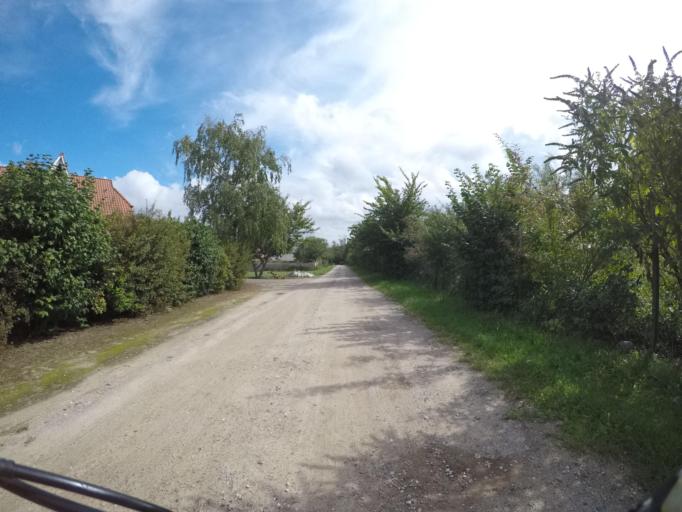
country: DE
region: Lower Saxony
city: Neu Darchau
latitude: 53.2410
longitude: 10.8905
